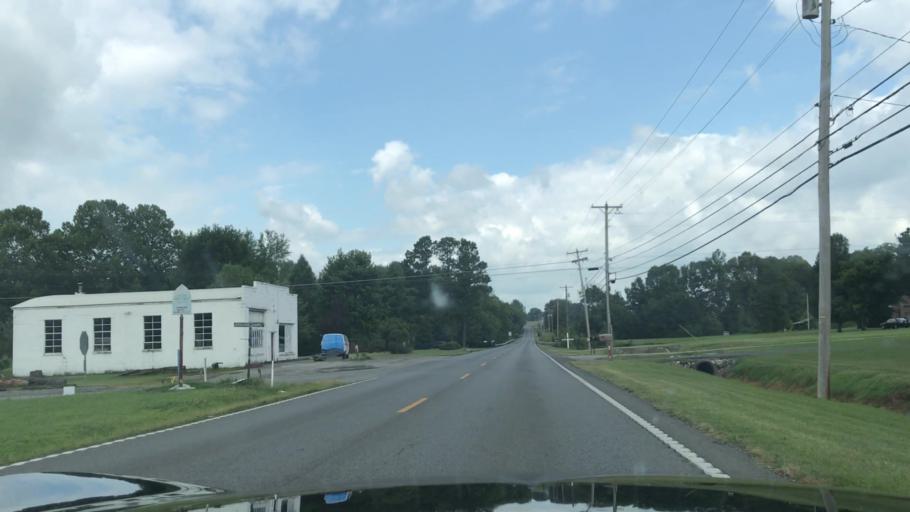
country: US
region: Kentucky
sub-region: Muhlenberg County
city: Greenville
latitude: 37.2006
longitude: -87.1360
